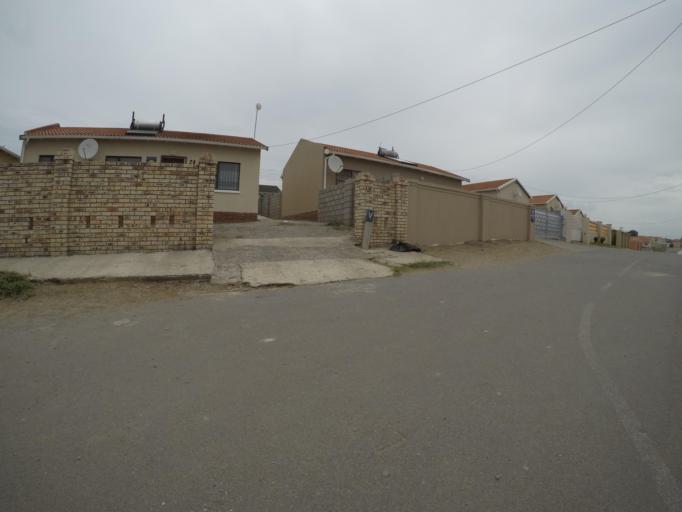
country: ZA
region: Eastern Cape
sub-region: Buffalo City Metropolitan Municipality
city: East London
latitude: -33.0038
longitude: 27.8556
